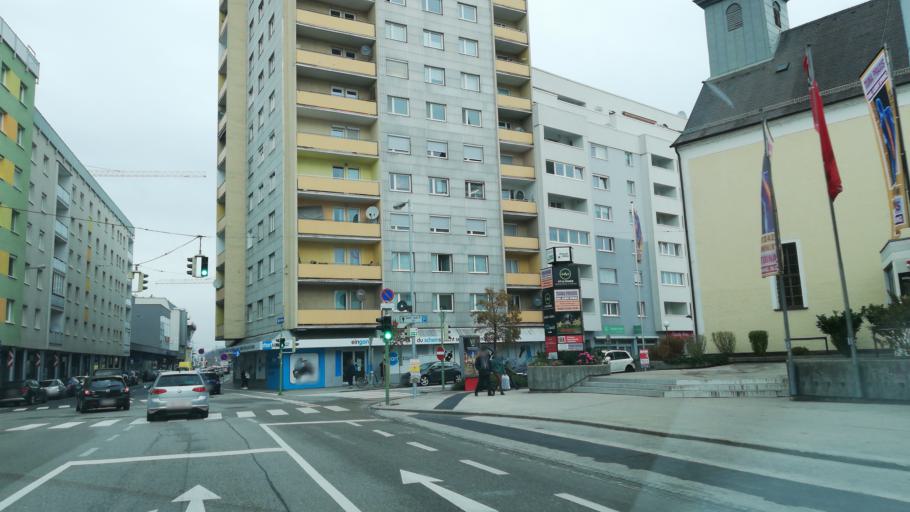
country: AT
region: Upper Austria
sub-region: Wels Stadt
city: Wels
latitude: 48.1590
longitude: 14.0279
